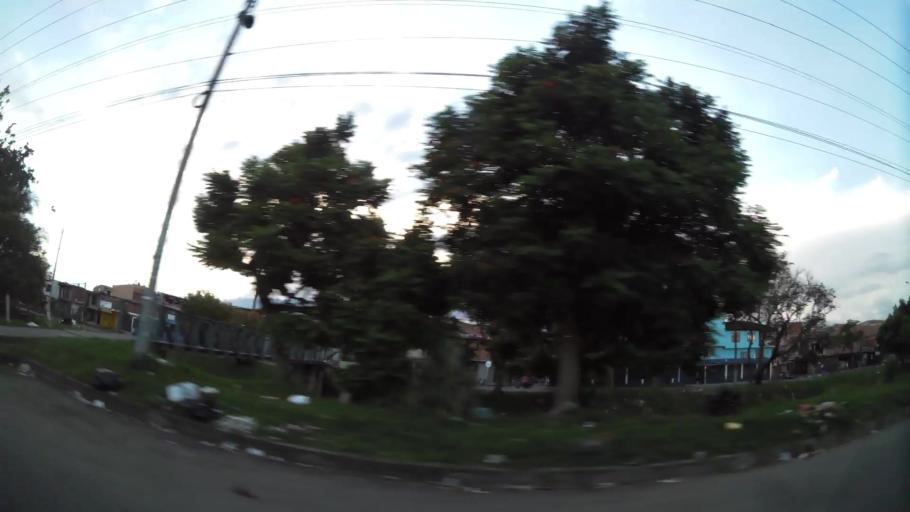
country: CO
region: Valle del Cauca
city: Cali
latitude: 3.4300
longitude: -76.4836
